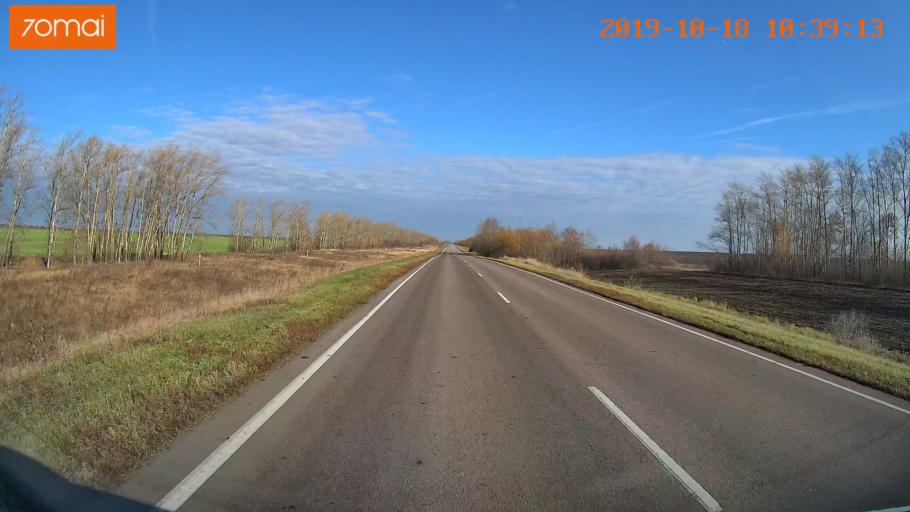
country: RU
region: Tula
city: Kurkino
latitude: 53.5836
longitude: 38.6502
